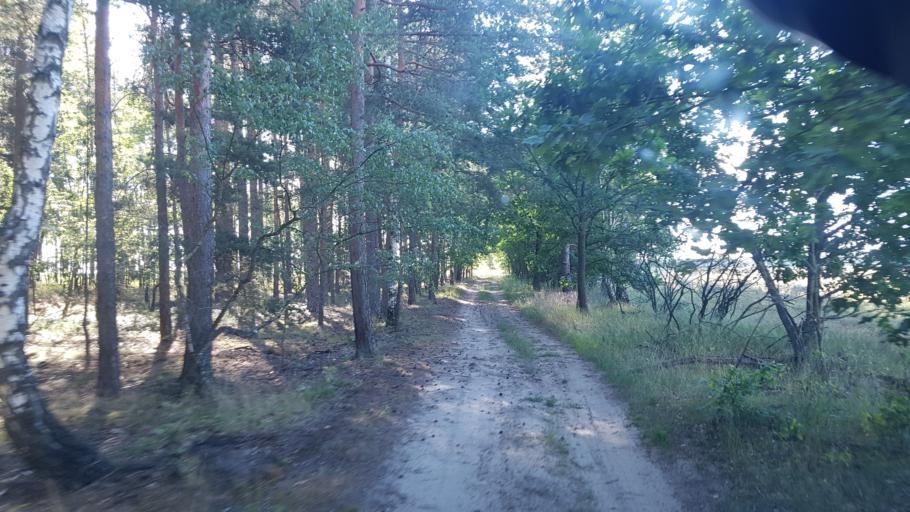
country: DE
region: Brandenburg
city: Sallgast
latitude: 51.6066
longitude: 13.7863
